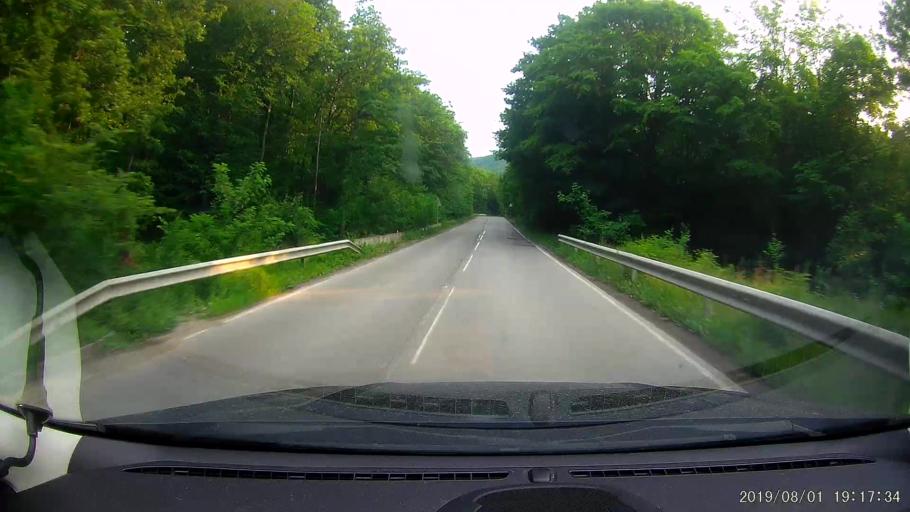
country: BG
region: Shumen
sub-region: Obshtina Smyadovo
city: Smyadovo
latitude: 42.9219
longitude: 26.9412
